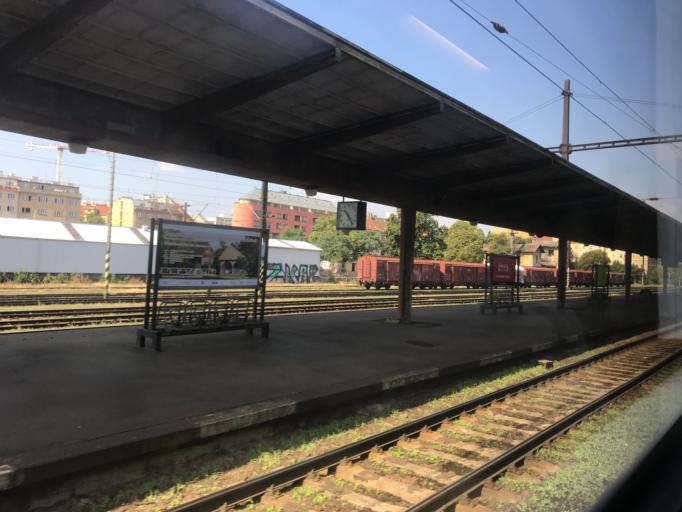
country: CZ
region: Praha
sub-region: Praha 8
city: Karlin
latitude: 50.0642
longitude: 14.4488
